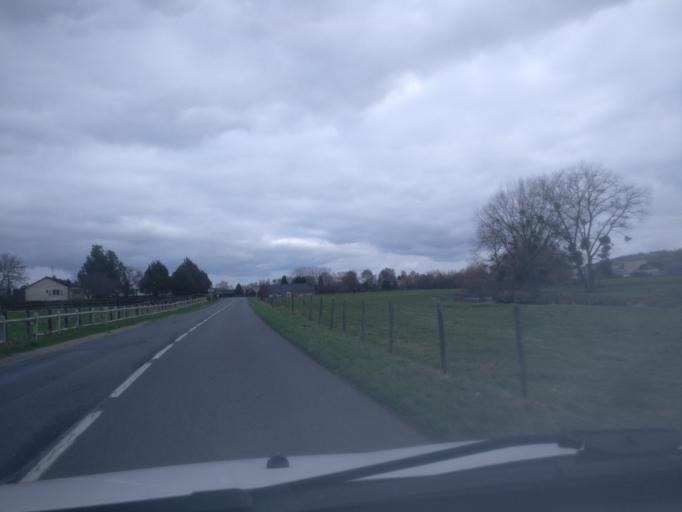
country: FR
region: Lower Normandy
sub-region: Departement de la Manche
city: Avranches
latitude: 48.6906
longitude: -1.3784
